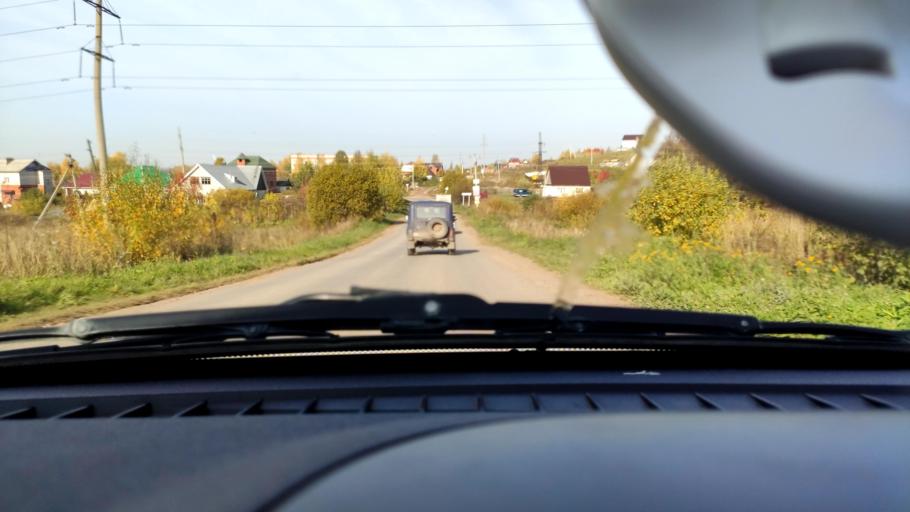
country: RU
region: Perm
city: Overyata
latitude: 58.0810
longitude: 55.8854
